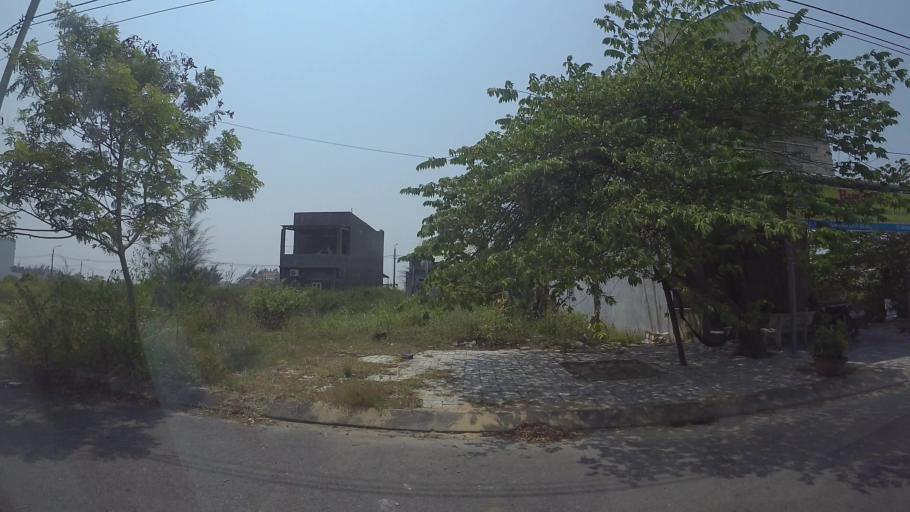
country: VN
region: Da Nang
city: Ngu Hanh Son
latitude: 15.9873
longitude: 108.2672
